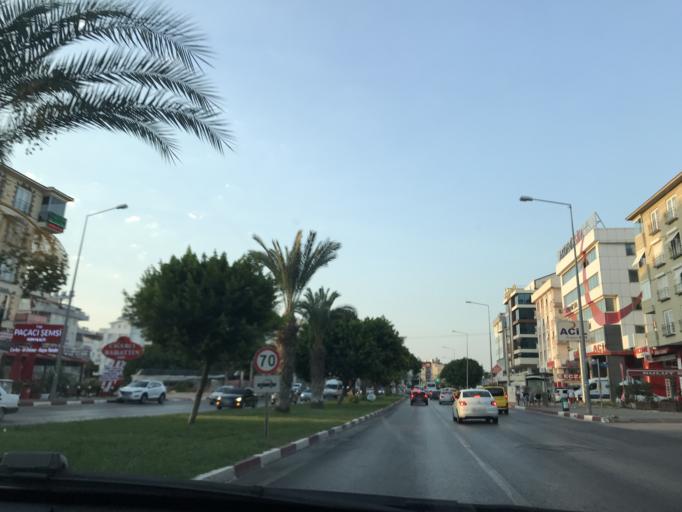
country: TR
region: Antalya
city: Antalya
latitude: 36.8728
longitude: 30.6420
